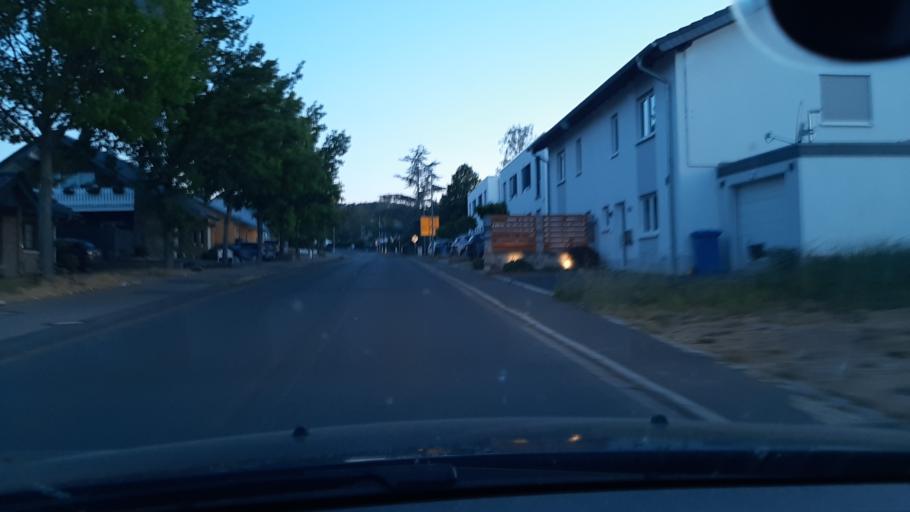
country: DE
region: North Rhine-Westphalia
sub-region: Regierungsbezirk Koln
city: Mechernich
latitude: 50.6114
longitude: 6.6551
